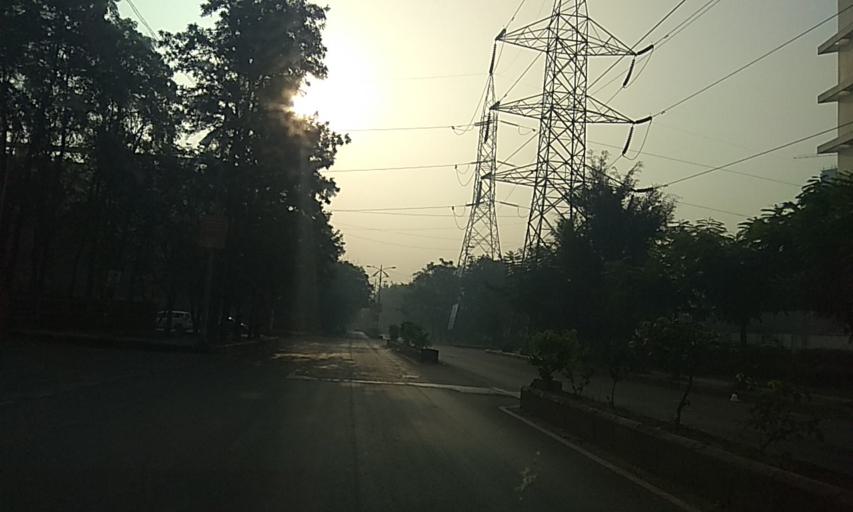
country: IN
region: Maharashtra
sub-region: Pune Division
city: Pimpri
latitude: 18.5847
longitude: 73.7348
